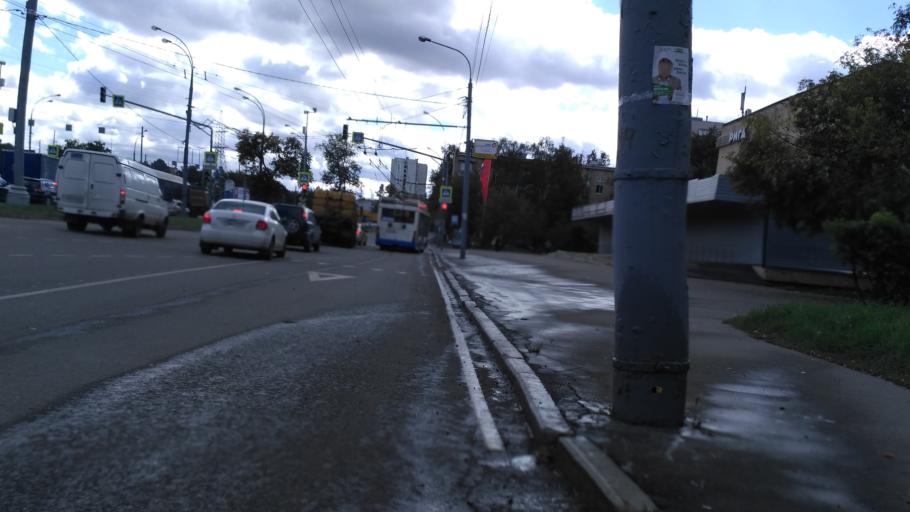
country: RU
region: Moscow
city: Novovladykino
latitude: 55.8455
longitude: 37.5843
